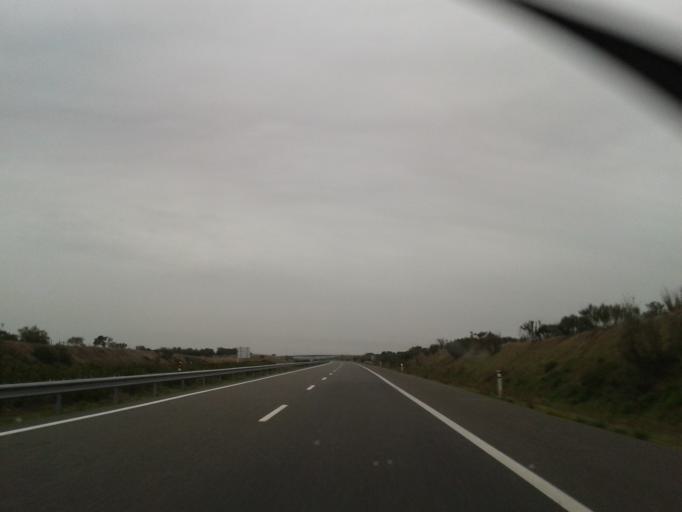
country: PT
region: Beja
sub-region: Ourique
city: Ourique
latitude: 37.6235
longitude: -8.1597
